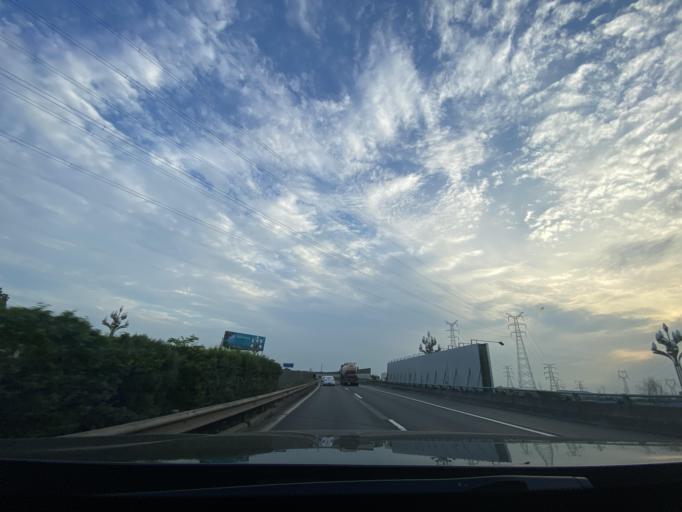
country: CN
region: Sichuan
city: Deyang
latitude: 31.0804
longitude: 104.3844
